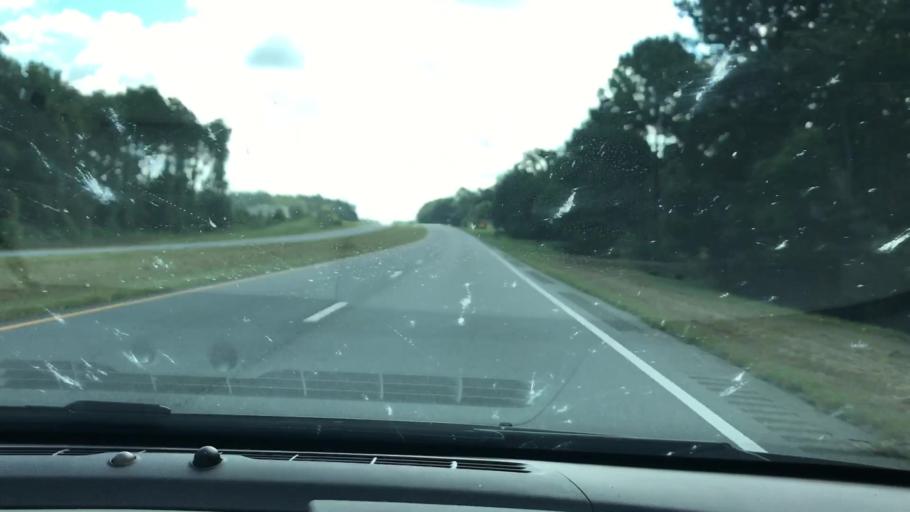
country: US
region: Georgia
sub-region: Worth County
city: Sylvester
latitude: 31.5517
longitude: -83.9420
